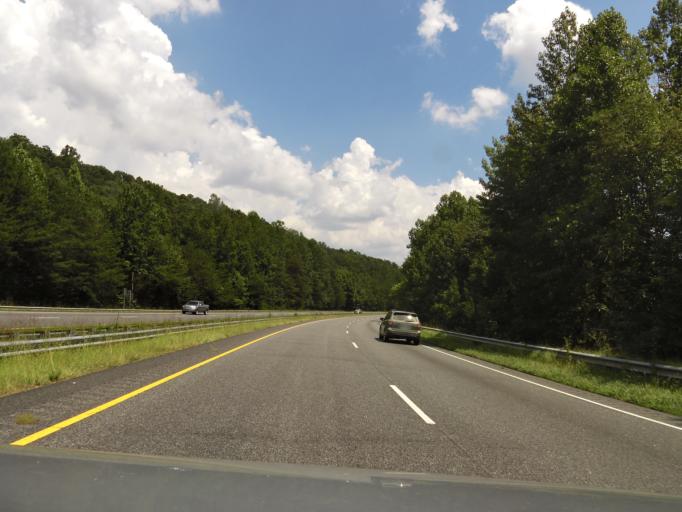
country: US
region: North Carolina
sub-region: Polk County
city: Columbus
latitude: 35.2590
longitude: -82.1937
